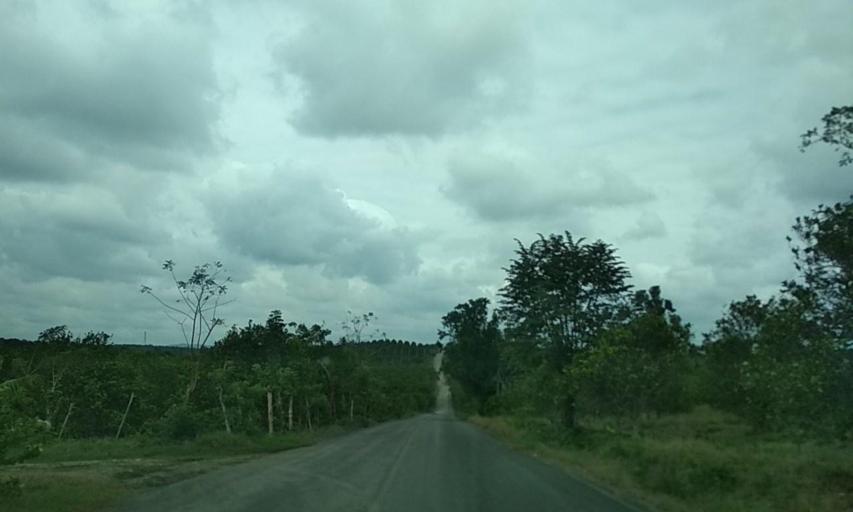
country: MX
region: Veracruz
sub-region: Papantla
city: El Chote
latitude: 20.3386
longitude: -97.3957
